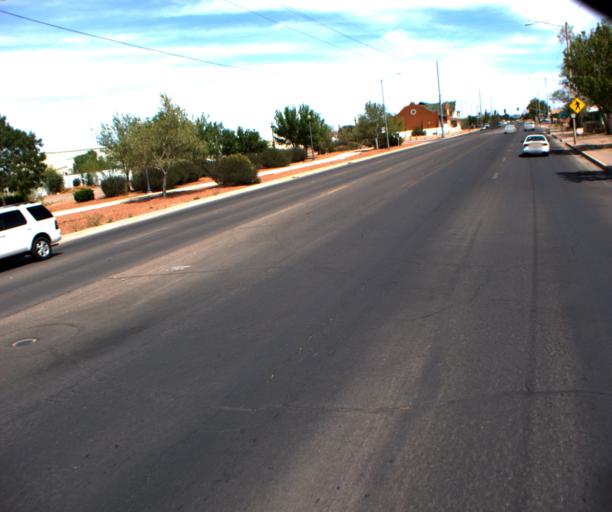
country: US
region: Arizona
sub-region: Cochise County
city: Douglas
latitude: 31.3423
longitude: -109.5578
